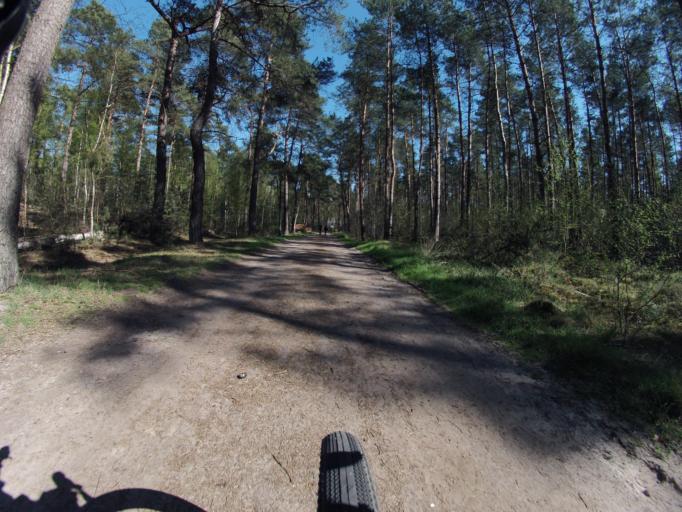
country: NL
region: Overijssel
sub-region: Gemeente Losser
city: Losser
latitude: 52.3331
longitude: 7.0406
